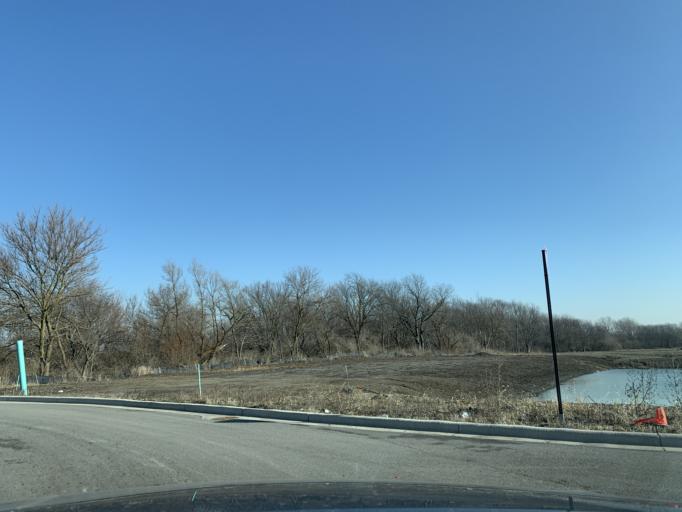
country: US
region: Indiana
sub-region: Lake County
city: Crown Point
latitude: 41.4272
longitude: -87.3336
